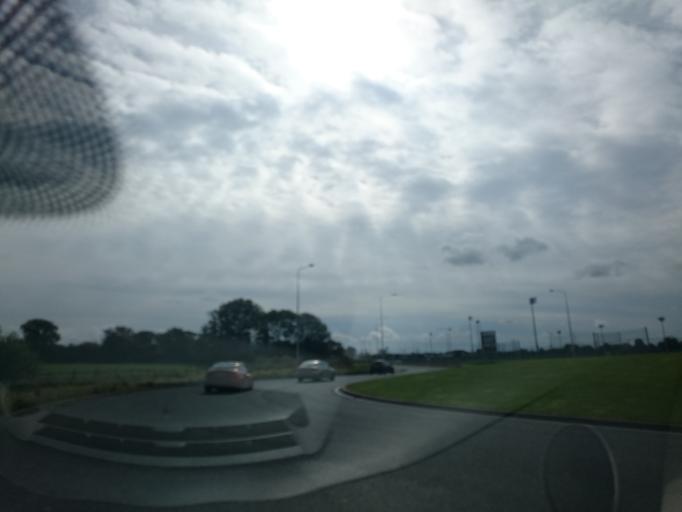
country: IE
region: Munster
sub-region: Waterford
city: Waterford
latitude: 52.2542
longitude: -7.1789
